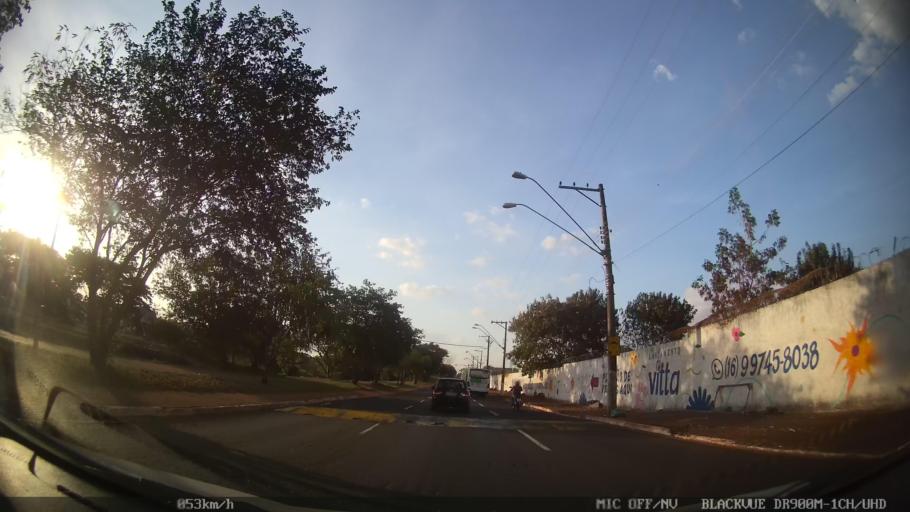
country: BR
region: Sao Paulo
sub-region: Ribeirao Preto
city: Ribeirao Preto
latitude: -21.1296
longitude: -47.8030
